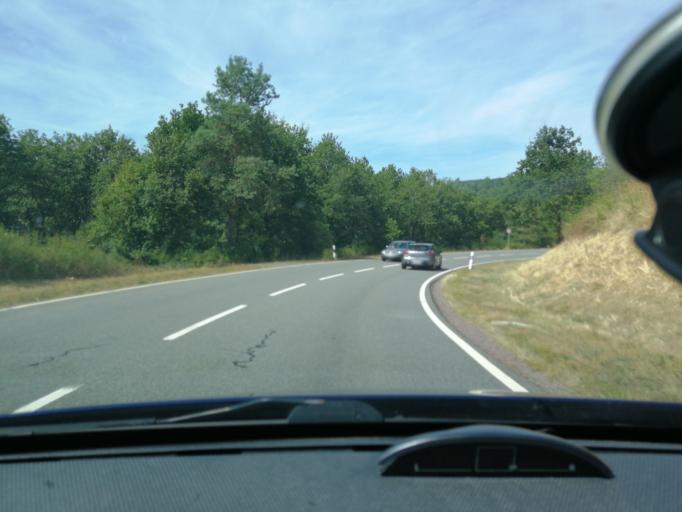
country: DE
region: Rheinland-Pfalz
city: Binsfeld
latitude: 49.9760
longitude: 6.7383
